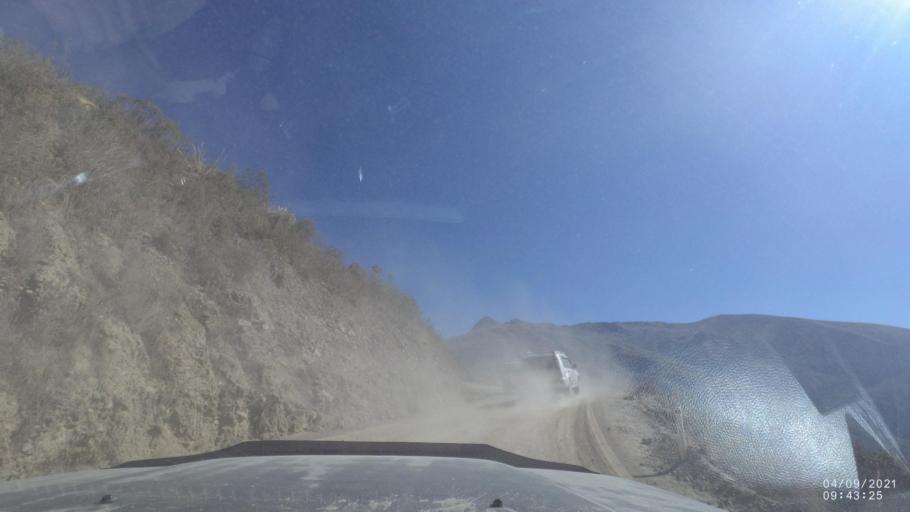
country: BO
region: Cochabamba
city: Sipe Sipe
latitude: -17.3394
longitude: -66.3907
